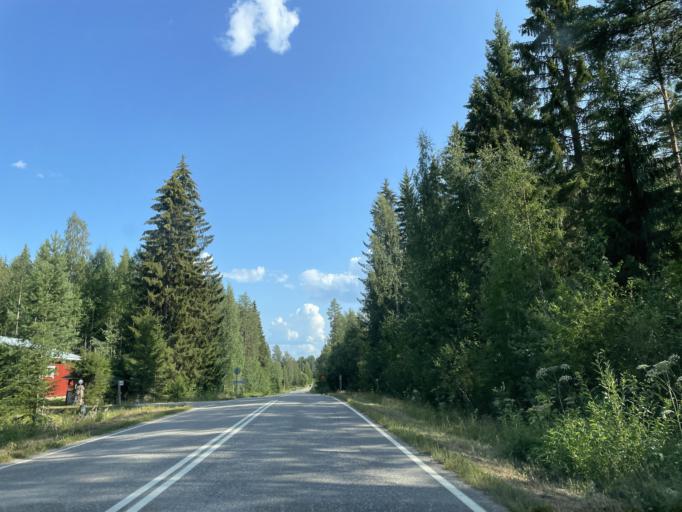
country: FI
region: Central Finland
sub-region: Saarijaervi-Viitasaari
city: Pihtipudas
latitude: 63.3635
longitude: 25.7408
